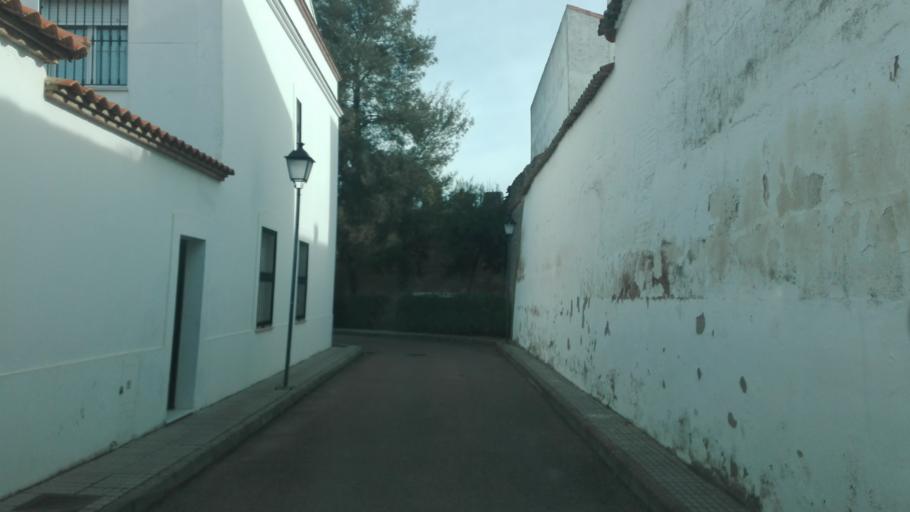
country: ES
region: Extremadura
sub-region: Provincia de Badajoz
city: Llerena
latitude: 38.2359
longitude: -6.0127
